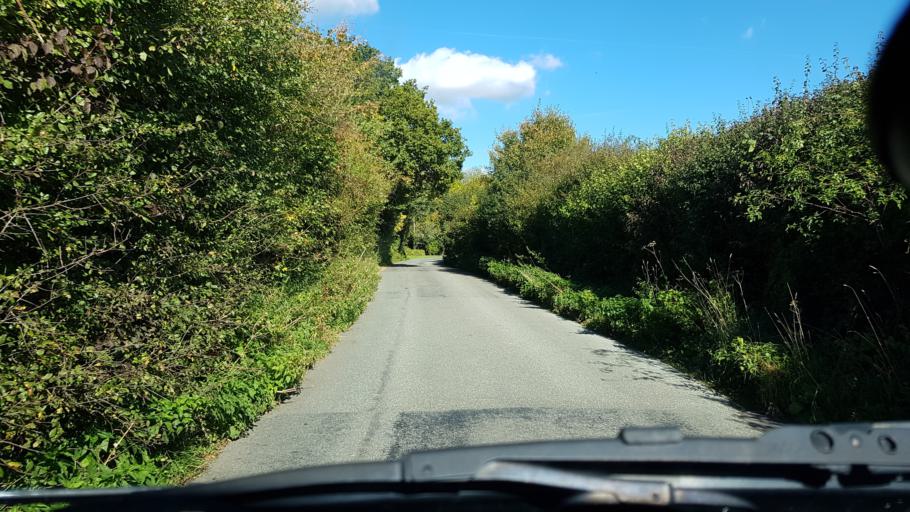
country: GB
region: England
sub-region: West Sussex
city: Billingshurst
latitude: 50.9987
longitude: -0.4335
